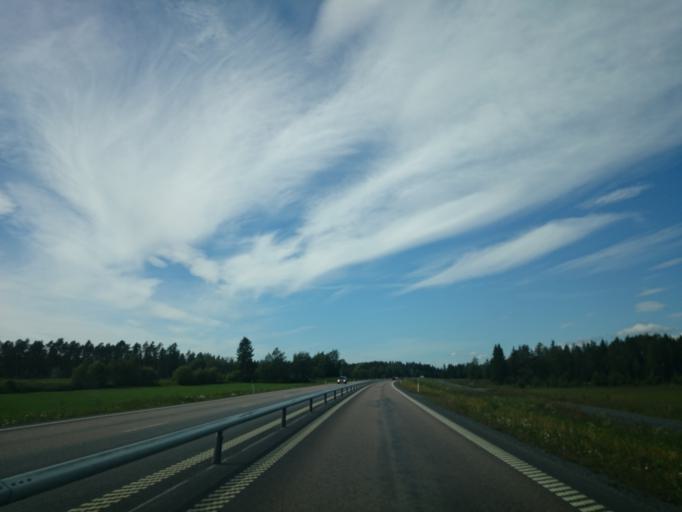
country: SE
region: Jaemtland
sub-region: OEstersunds Kommun
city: Ostersund
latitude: 63.2587
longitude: 14.5543
